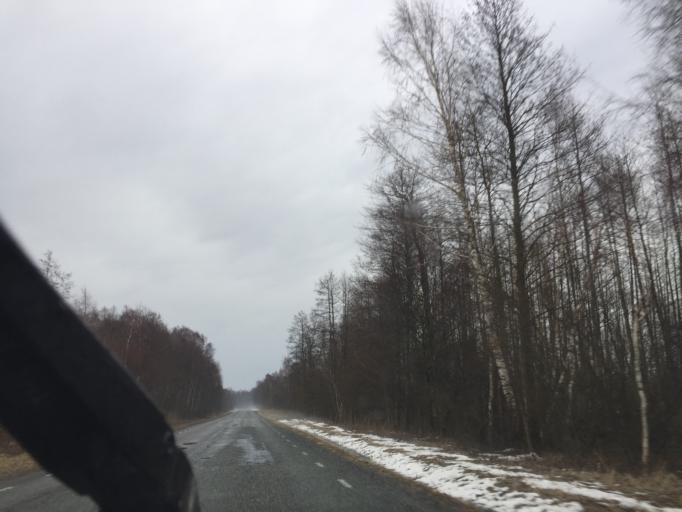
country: EE
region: Saare
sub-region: Orissaare vald
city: Orissaare
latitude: 58.5706
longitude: 23.0338
